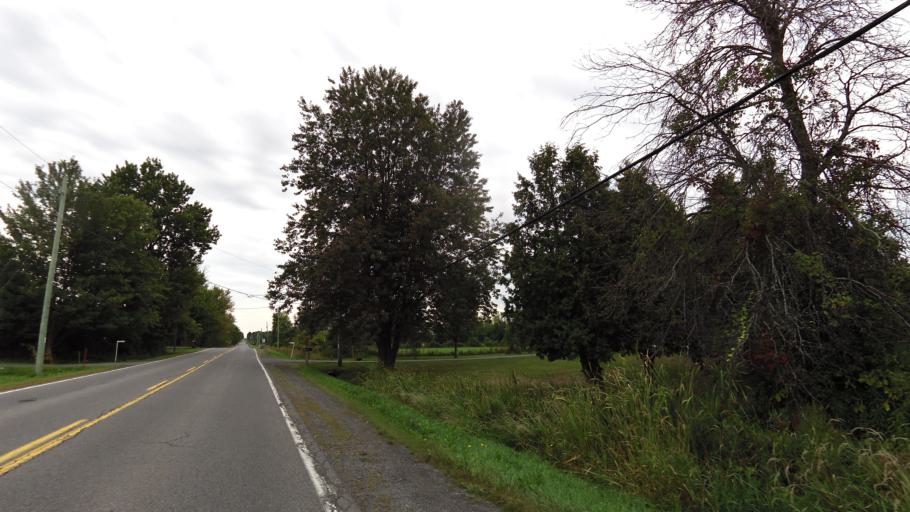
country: CA
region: Ontario
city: Ottawa
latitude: 45.2241
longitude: -75.4667
